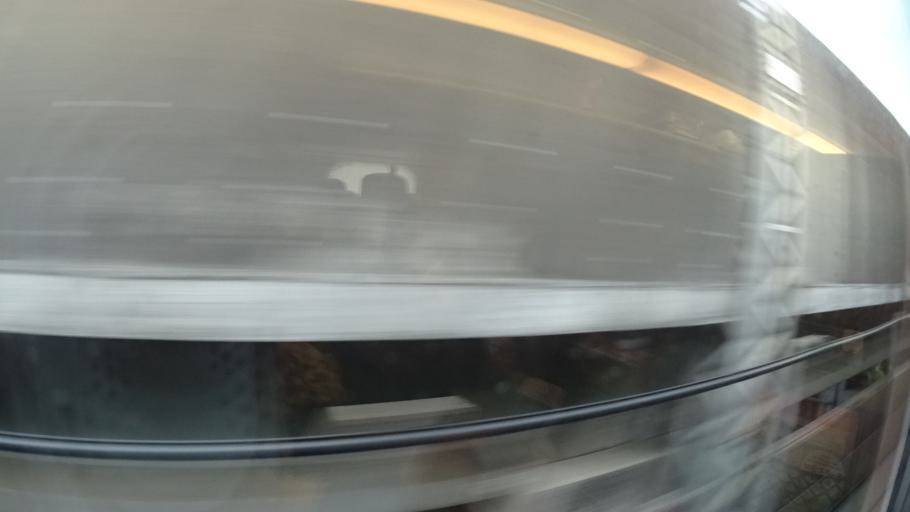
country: JP
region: Saitama
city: Ageoshimo
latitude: 35.9678
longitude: 139.6231
